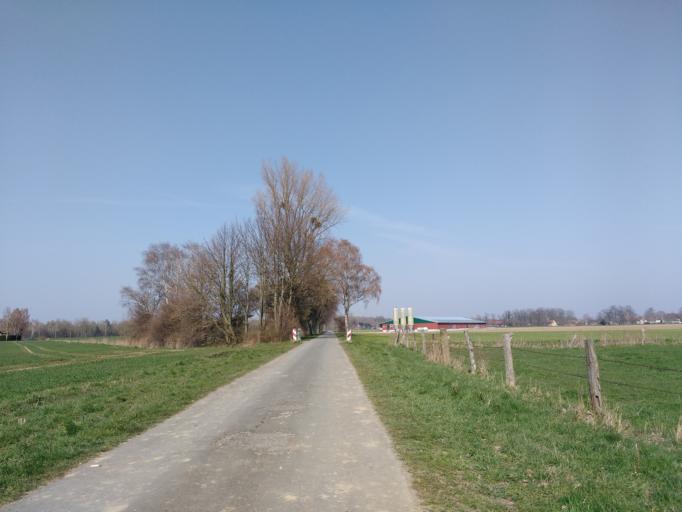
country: DE
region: North Rhine-Westphalia
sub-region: Regierungsbezirk Detmold
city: Salzkotten
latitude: 51.7318
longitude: 8.6534
